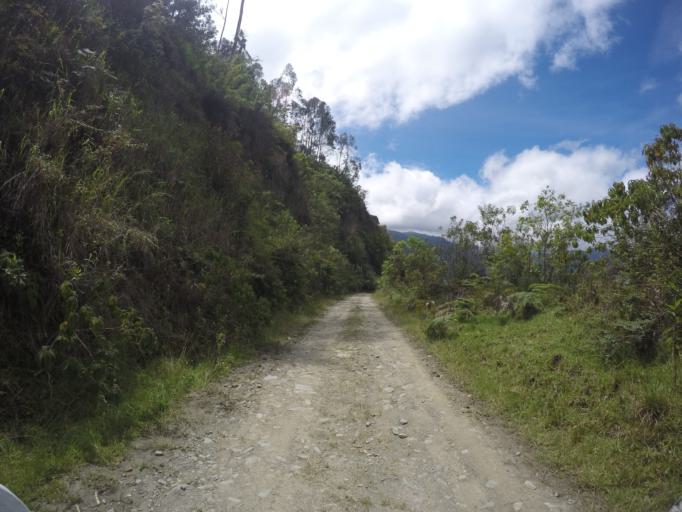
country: CO
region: Tolima
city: Cajamarca
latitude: 4.5331
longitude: -75.4272
